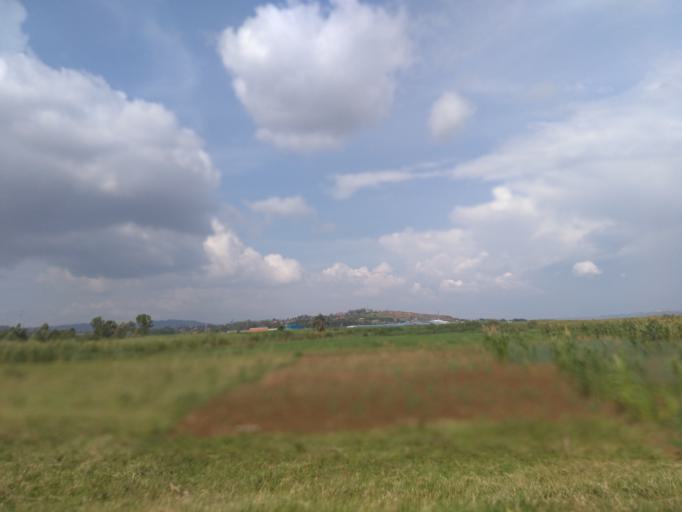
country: UG
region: Eastern Region
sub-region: Jinja District
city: Jinja
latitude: 0.4233
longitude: 33.2224
